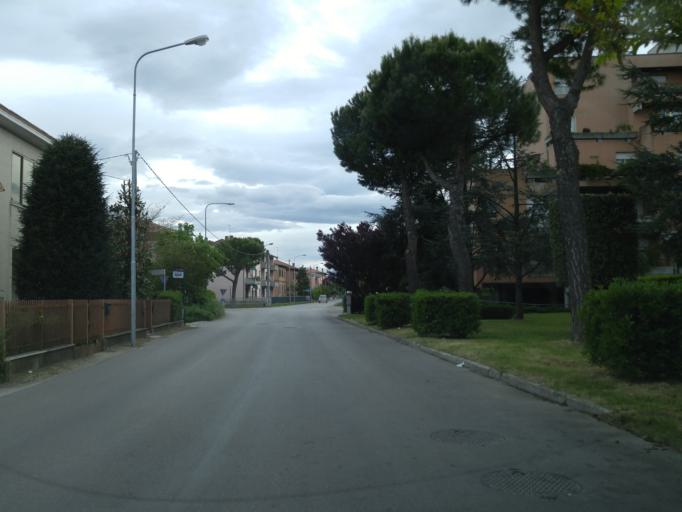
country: IT
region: The Marches
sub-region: Provincia di Pesaro e Urbino
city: Fano
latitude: 43.8319
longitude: 13.0064
